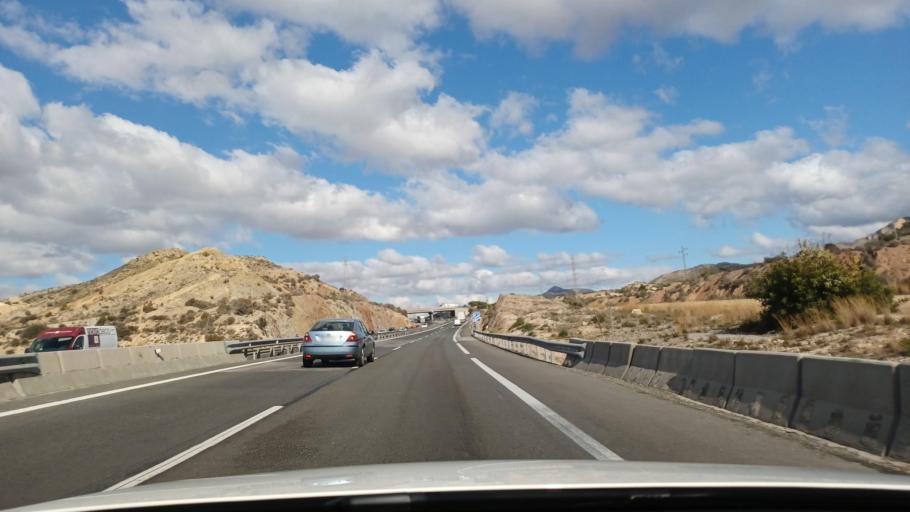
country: ES
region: Valencia
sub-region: Provincia de Alicante
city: Novelda
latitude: 38.4274
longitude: -0.7826
